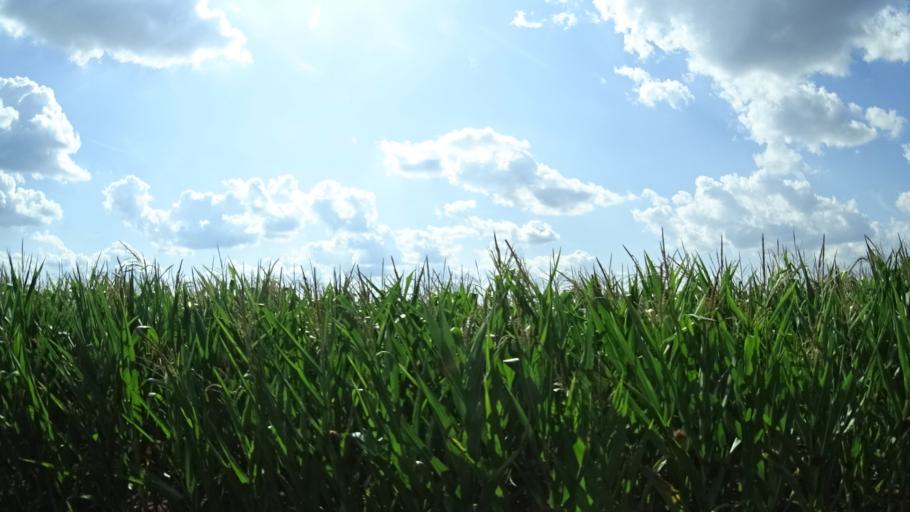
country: DE
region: Bavaria
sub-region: Regierungsbezirk Unterfranken
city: Trappstadt
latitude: 50.2876
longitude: 10.5854
